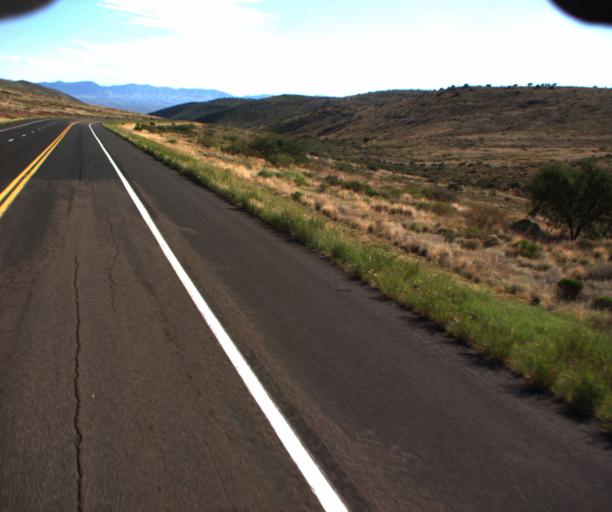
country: US
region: Arizona
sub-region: Greenlee County
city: Clifton
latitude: 32.8694
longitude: -109.2904
